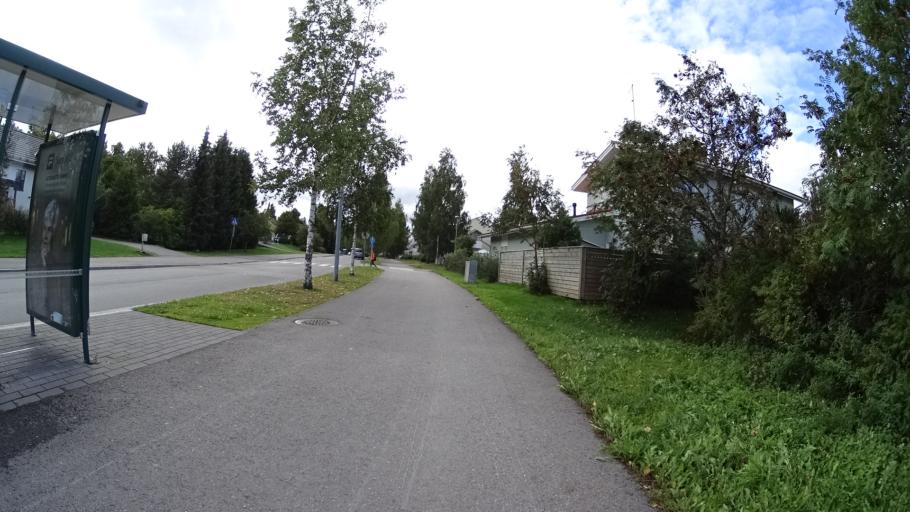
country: FI
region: Uusimaa
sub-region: Helsinki
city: Vantaa
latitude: 60.2649
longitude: 24.9549
